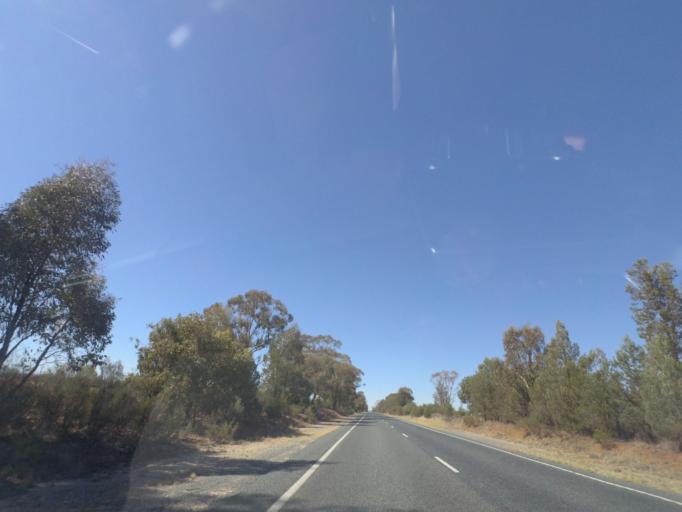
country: AU
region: New South Wales
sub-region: Bland
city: West Wyalong
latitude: -34.1569
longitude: 147.1174
